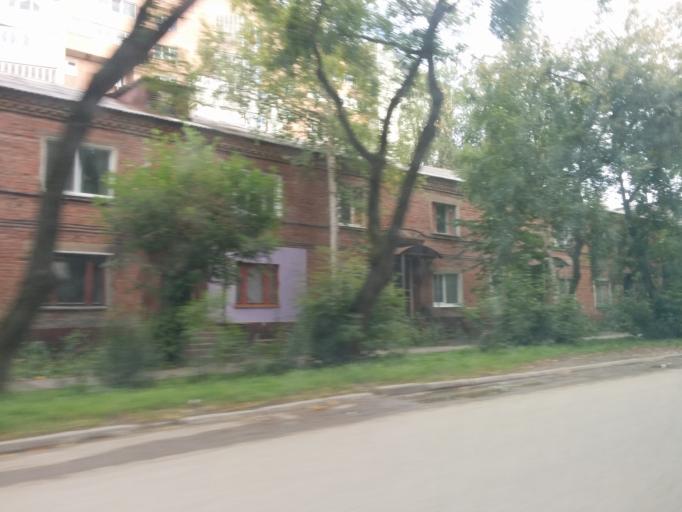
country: RU
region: Perm
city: Perm
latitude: 58.0006
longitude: 56.3001
